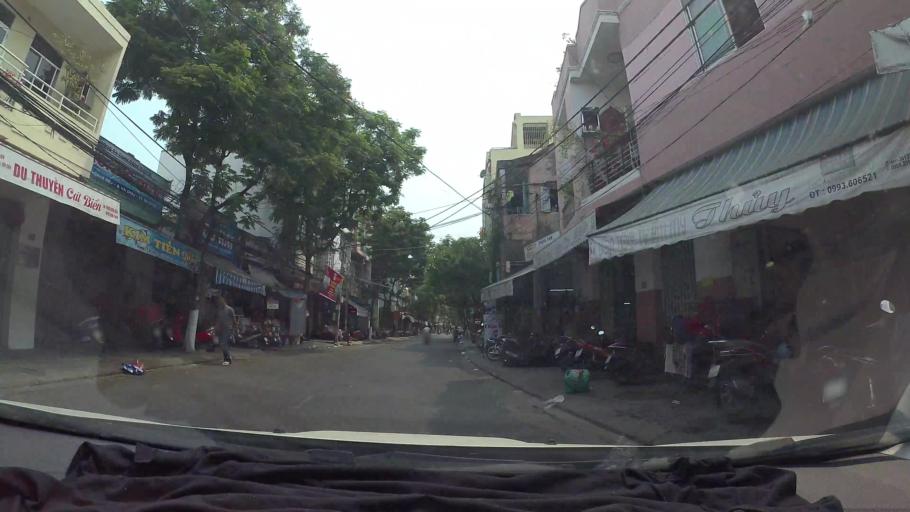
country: VN
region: Da Nang
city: Da Nang
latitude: 16.0517
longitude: 108.2179
